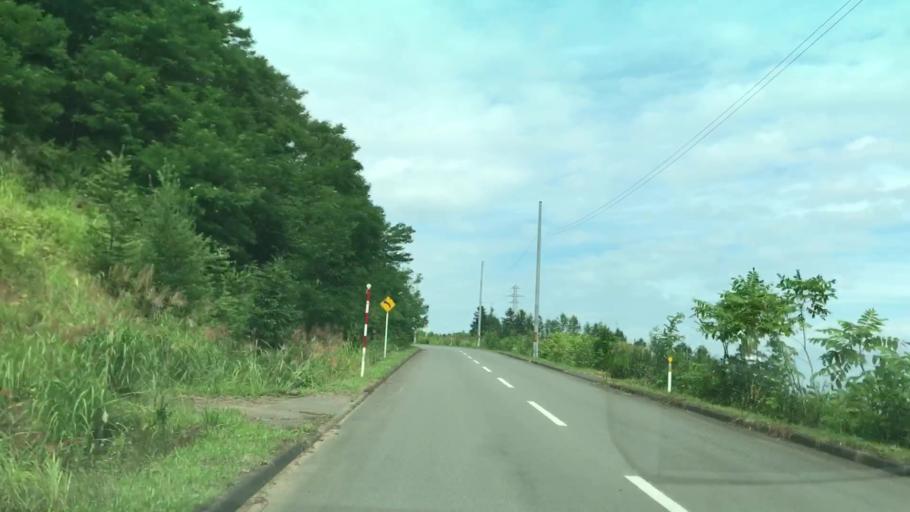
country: JP
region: Hokkaido
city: Yoichi
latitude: 43.1778
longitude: 140.8429
